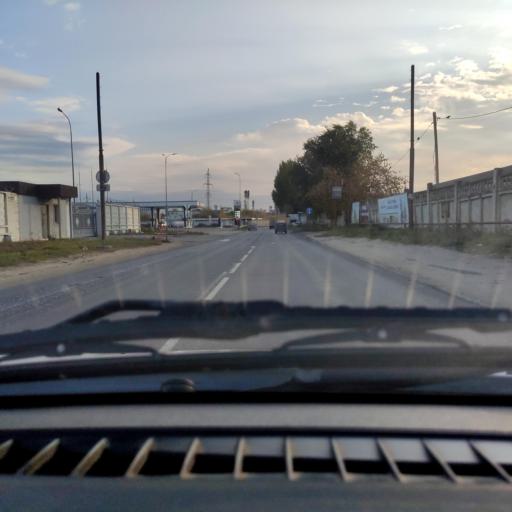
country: RU
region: Samara
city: Tol'yatti
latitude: 53.5356
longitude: 49.4336
